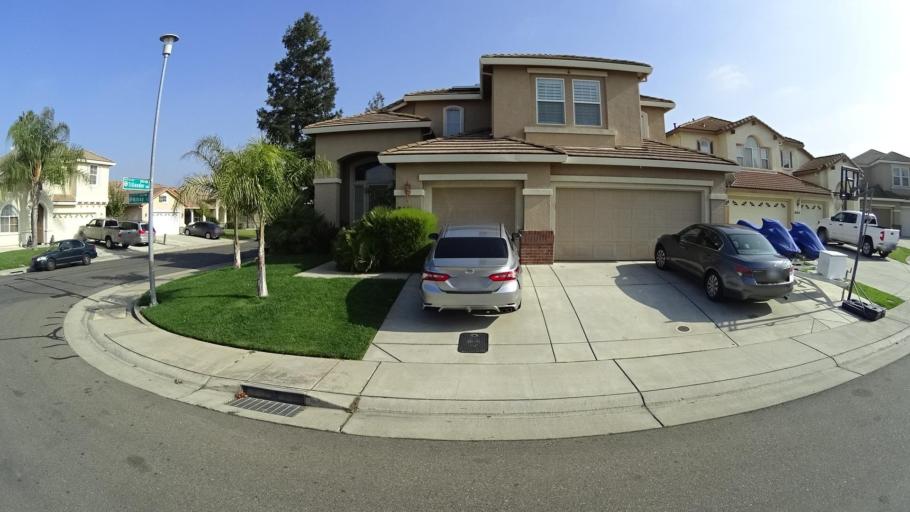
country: US
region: California
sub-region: Sacramento County
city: Vineyard
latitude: 38.4467
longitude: -121.3647
